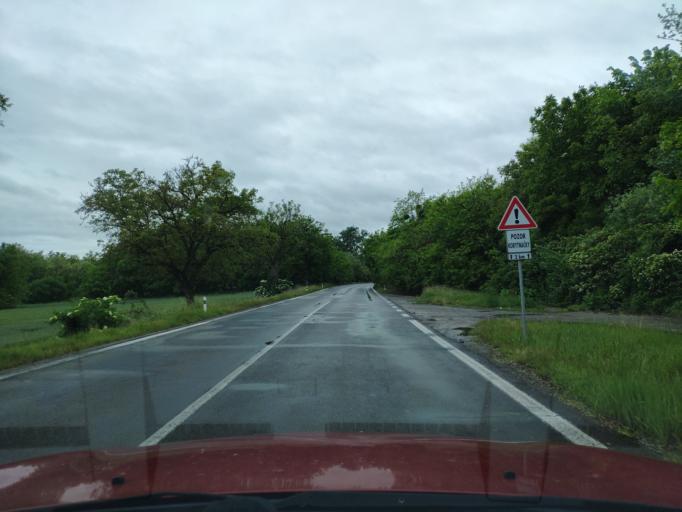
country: HU
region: Borsod-Abauj-Zemplen
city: Karcsa
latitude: 48.3899
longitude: 21.7915
